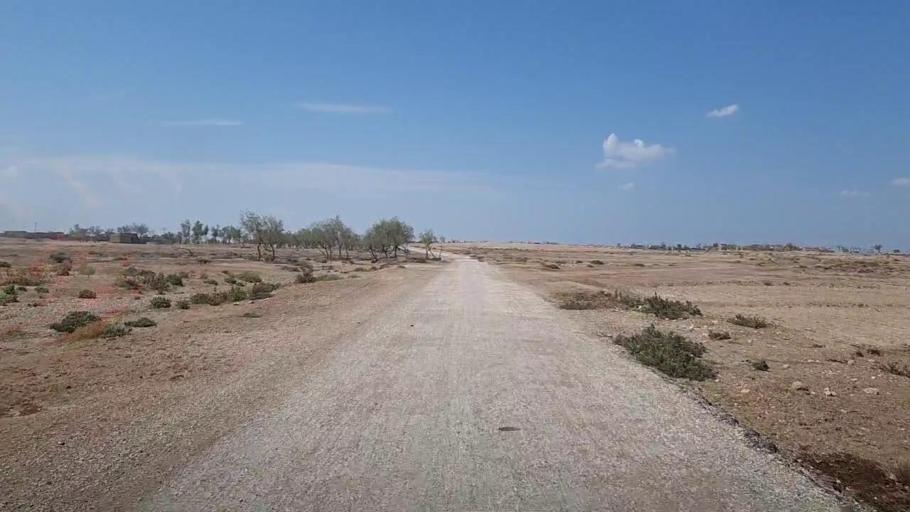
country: PK
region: Sindh
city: Sehwan
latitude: 26.3487
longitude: 67.6738
